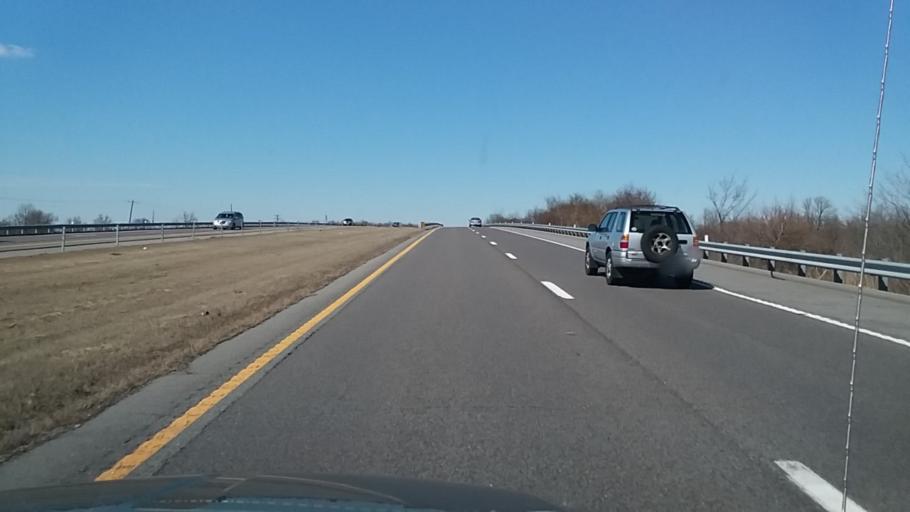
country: US
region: Missouri
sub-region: Scott County
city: Benton
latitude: 37.0057
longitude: -89.5349
